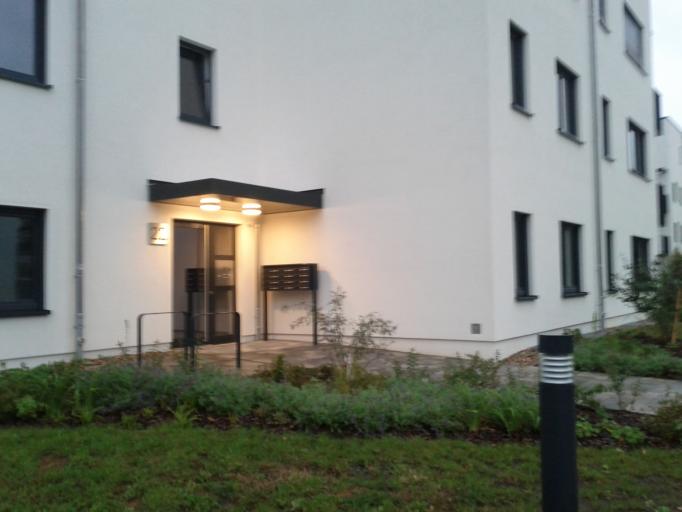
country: DE
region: Berlin
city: Zehlendorf Bezirk
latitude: 52.4482
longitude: 13.2666
